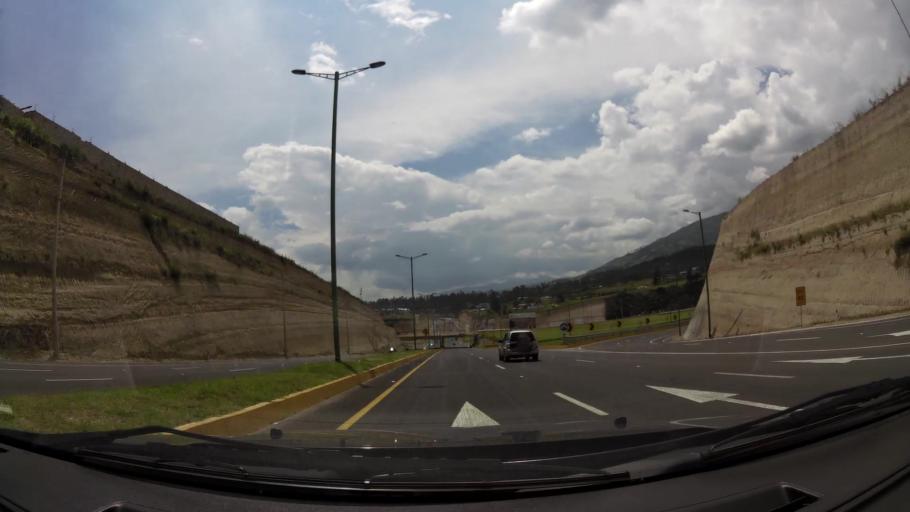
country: EC
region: Pichincha
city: Sangolqui
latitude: -0.2155
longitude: -78.3352
